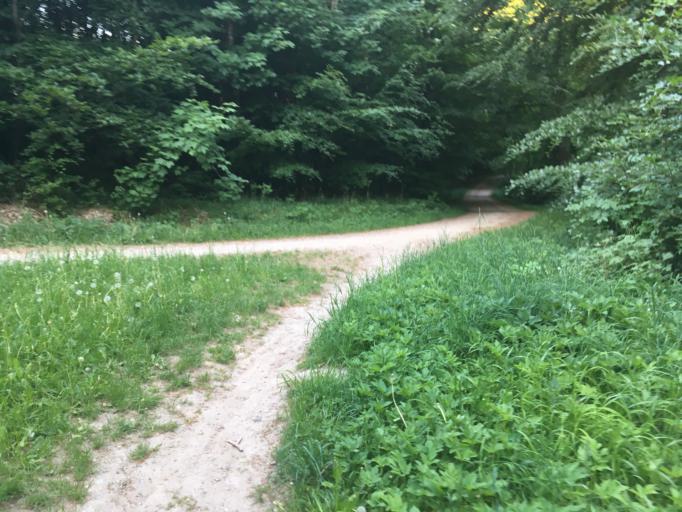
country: DK
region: Capital Region
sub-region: Ballerup Kommune
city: Ballerup
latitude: 55.7559
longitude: 12.3677
